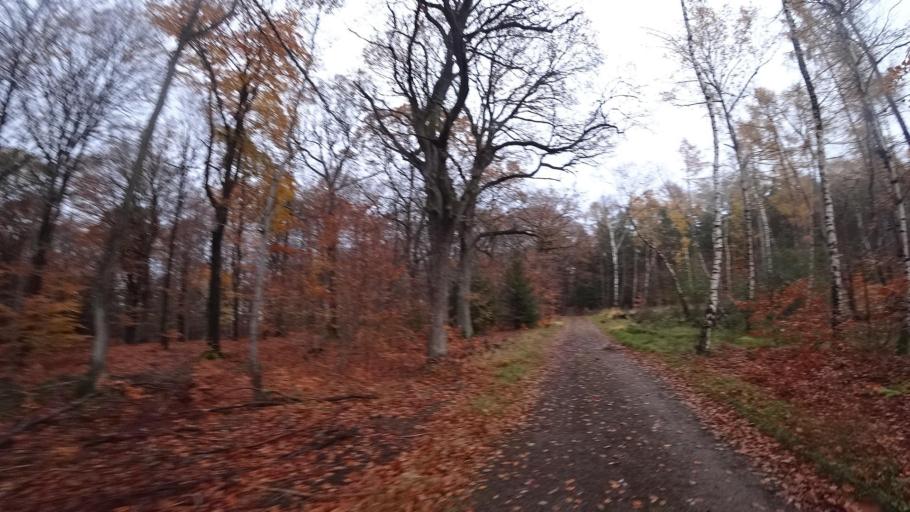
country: DE
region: Rheinland-Pfalz
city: Schalkenbach
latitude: 50.5052
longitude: 7.1221
